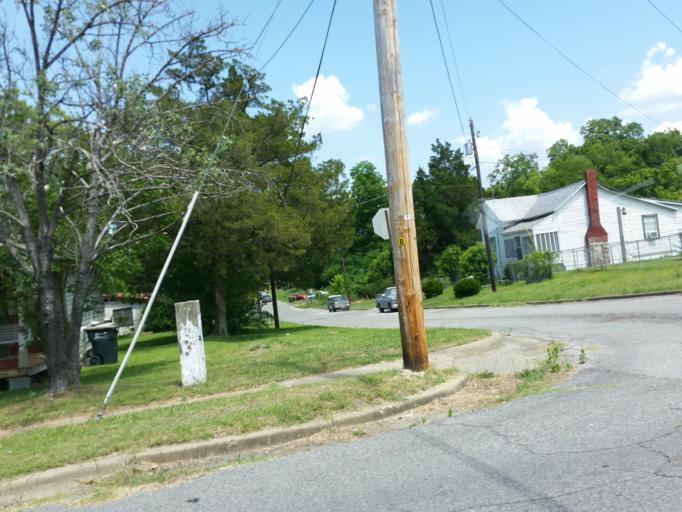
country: US
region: Alabama
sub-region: Marengo County
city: Demopolis
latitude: 32.5174
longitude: -87.8316
